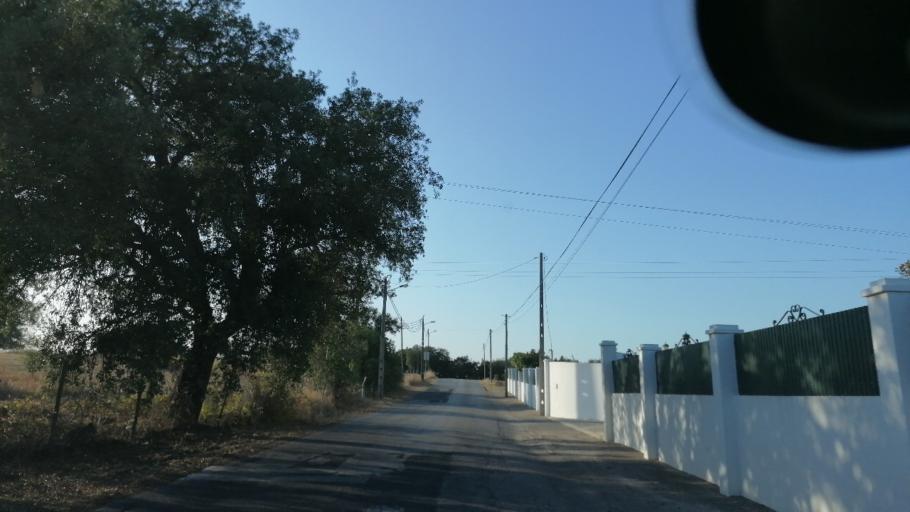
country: PT
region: Setubal
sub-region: Setubal
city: Setubal
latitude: 38.5475
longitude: -8.8412
